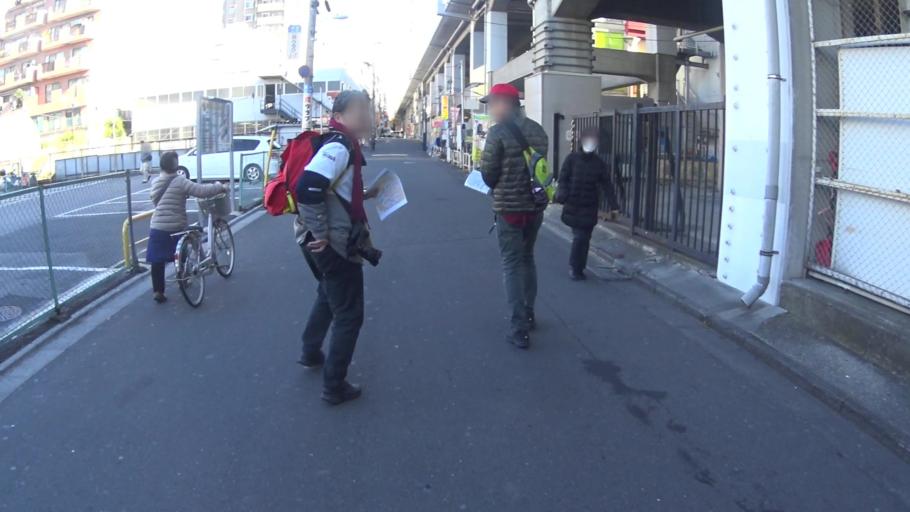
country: JP
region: Saitama
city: Shimotoda
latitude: 35.8482
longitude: 139.6693
